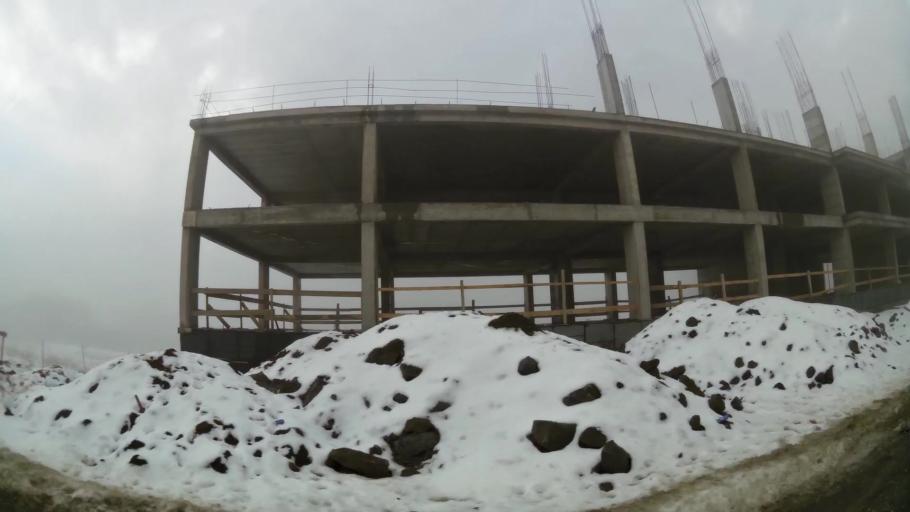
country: XK
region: Pristina
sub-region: Komuna e Prishtines
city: Pristina
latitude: 42.6407
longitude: 21.1509
